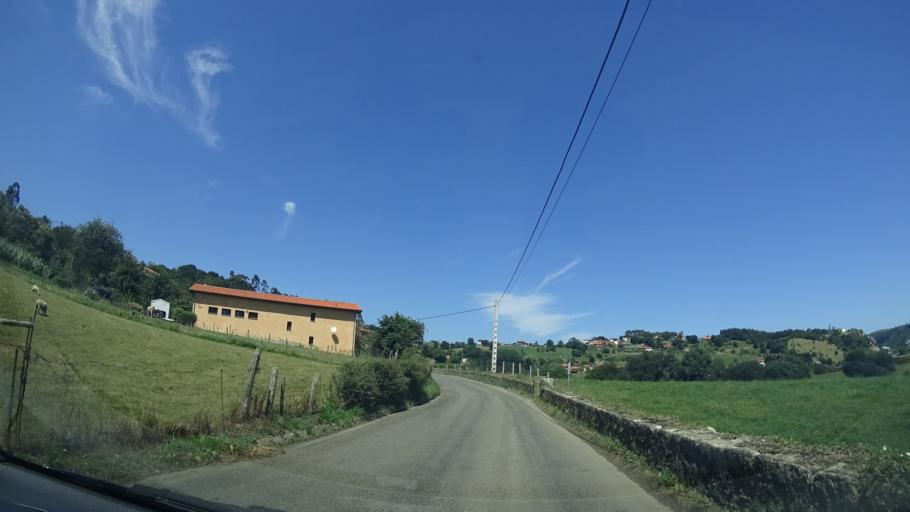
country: ES
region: Asturias
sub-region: Province of Asturias
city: Ribadesella
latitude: 43.4508
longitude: -5.0722
